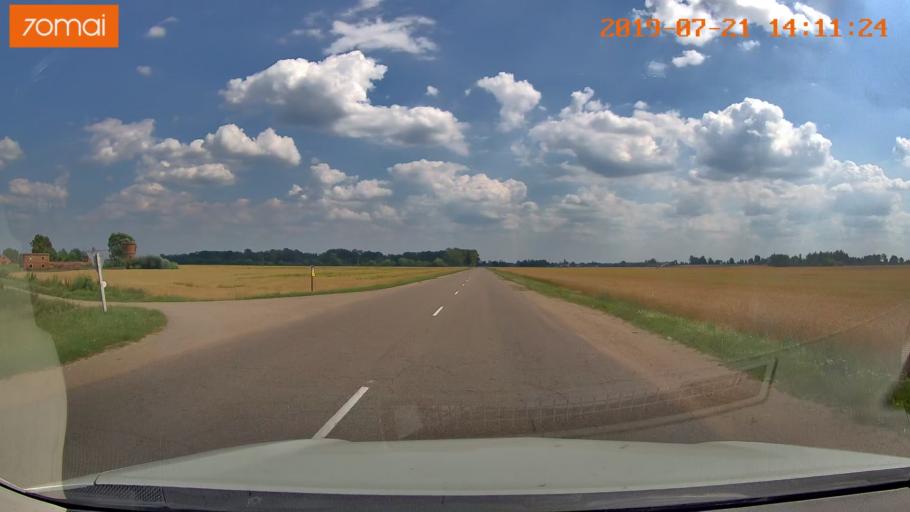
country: BY
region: Grodnenskaya
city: Karelichy
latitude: 53.6579
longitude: 26.1514
